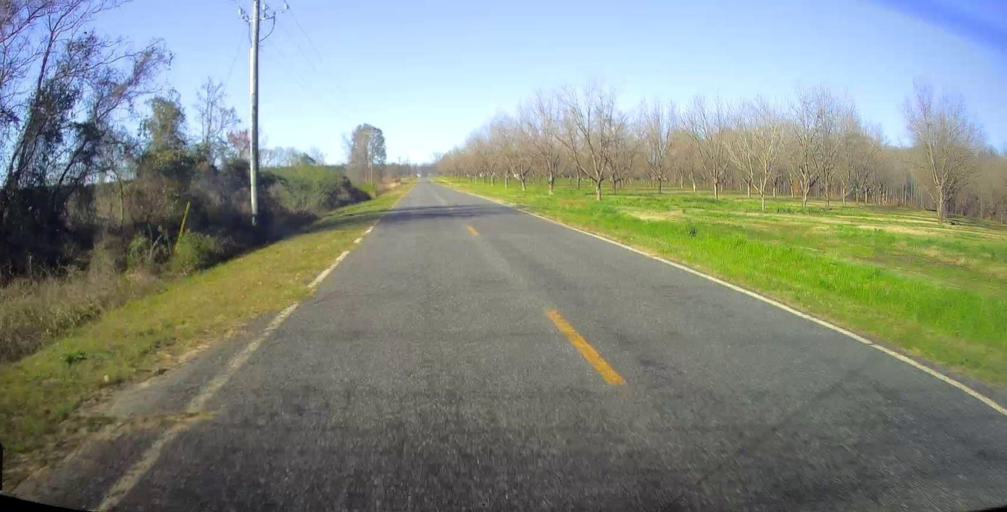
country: US
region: Georgia
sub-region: Peach County
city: Fort Valley
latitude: 32.6280
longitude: -83.8547
